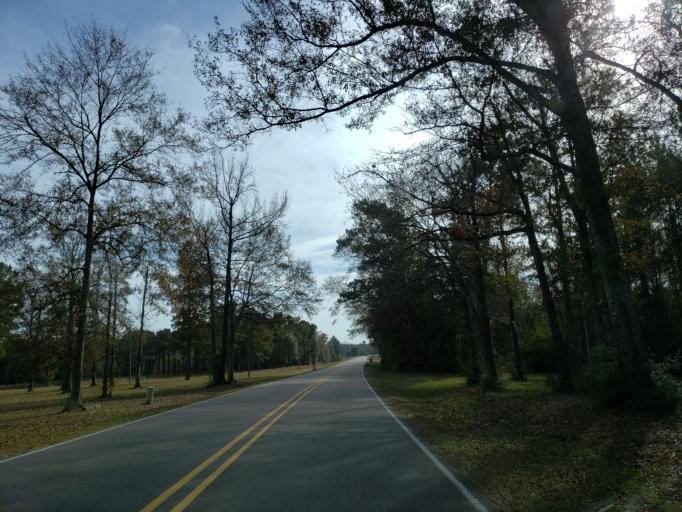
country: US
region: Mississippi
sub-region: Forrest County
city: Rawls Springs
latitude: 31.4002
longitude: -89.3651
